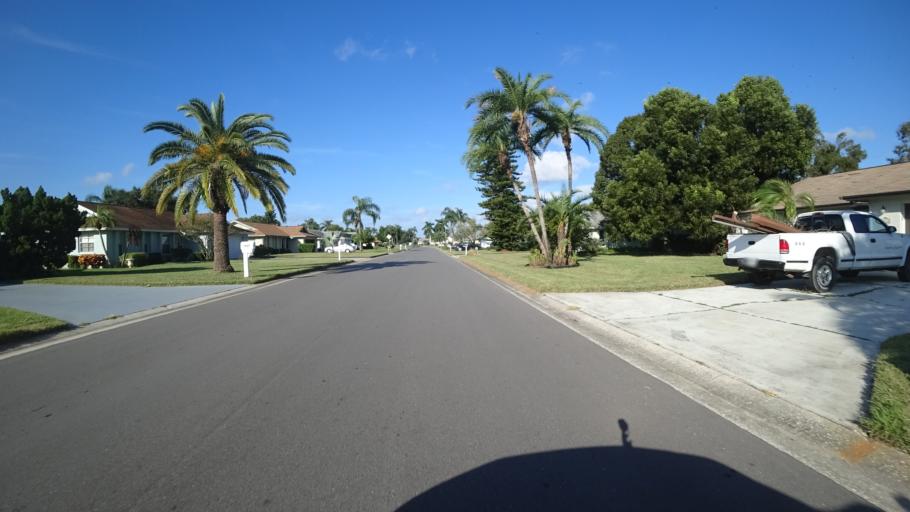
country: US
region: Florida
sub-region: Manatee County
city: West Bradenton
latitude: 27.4900
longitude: -82.6176
